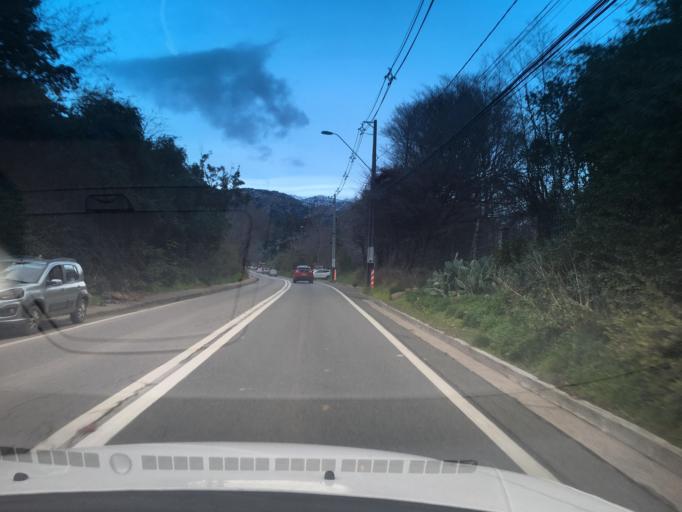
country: CL
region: Santiago Metropolitan
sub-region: Provincia de Cordillera
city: Puente Alto
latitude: -33.5814
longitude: -70.4070
